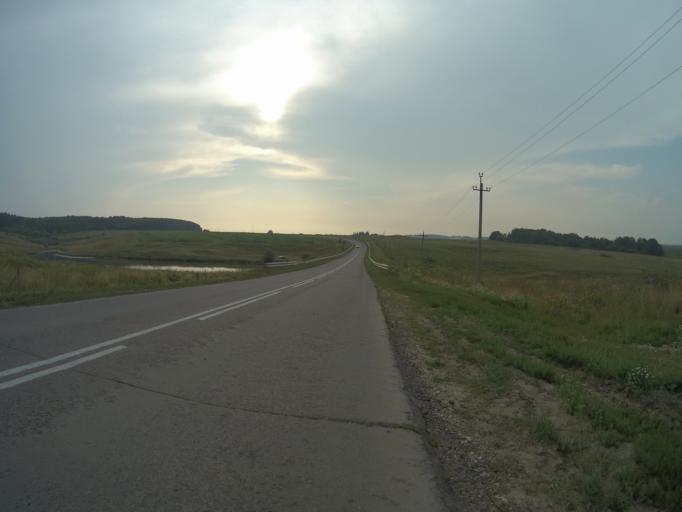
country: RU
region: Ivanovo
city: Gavrilov Posad
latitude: 56.3462
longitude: 40.1815
